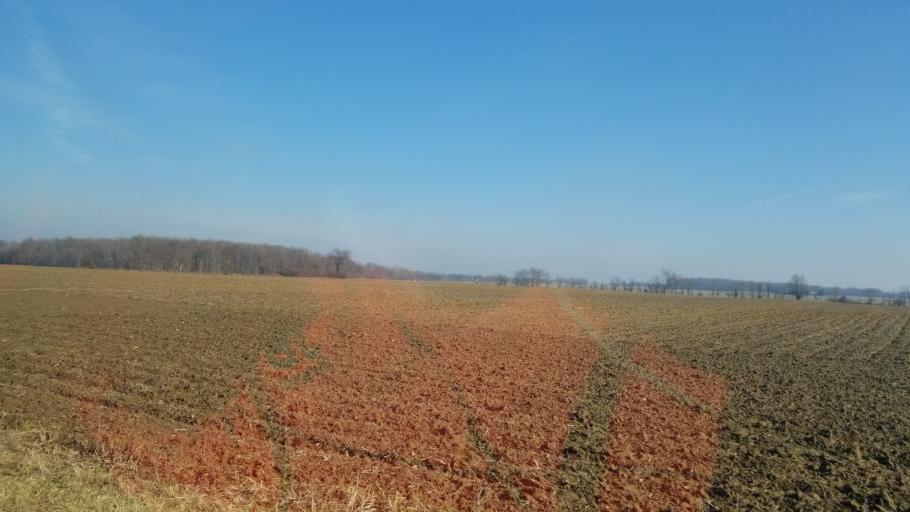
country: US
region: Ohio
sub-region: Seneca County
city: Tiffin
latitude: 41.0241
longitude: -83.0741
